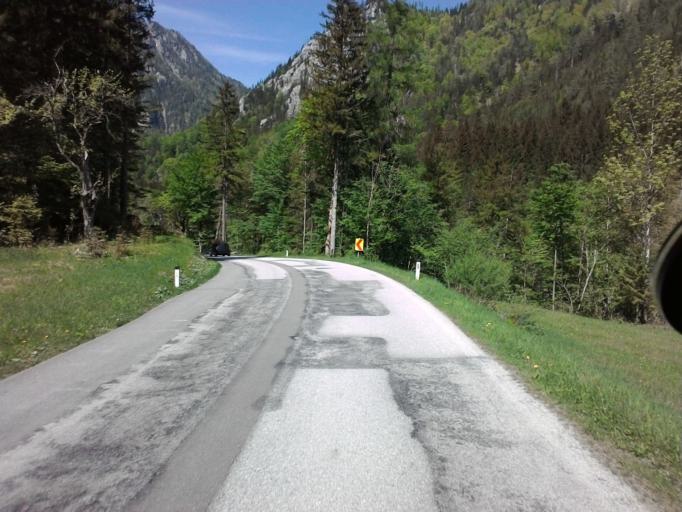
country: AT
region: Styria
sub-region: Politischer Bezirk Liezen
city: Wildalpen
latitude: 47.6888
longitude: 14.9013
